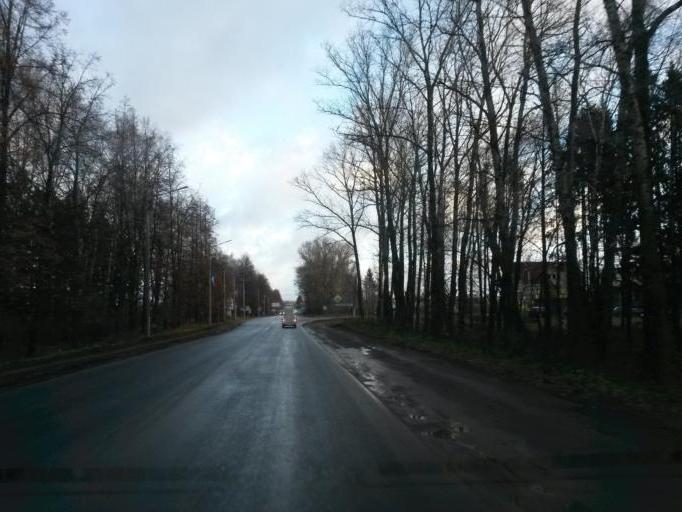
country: RU
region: Jaroslavl
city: Pereslavl'-Zalesskiy
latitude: 56.7566
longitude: 38.8662
